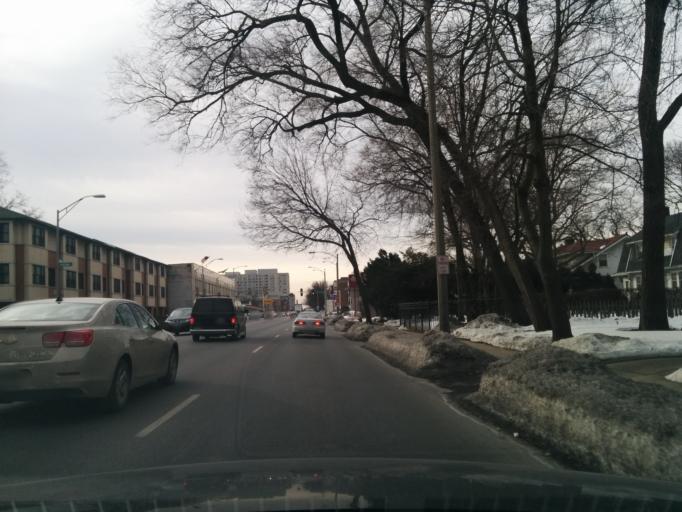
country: US
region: Illinois
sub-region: Cook County
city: River Forest
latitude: 41.8956
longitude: -87.8053
